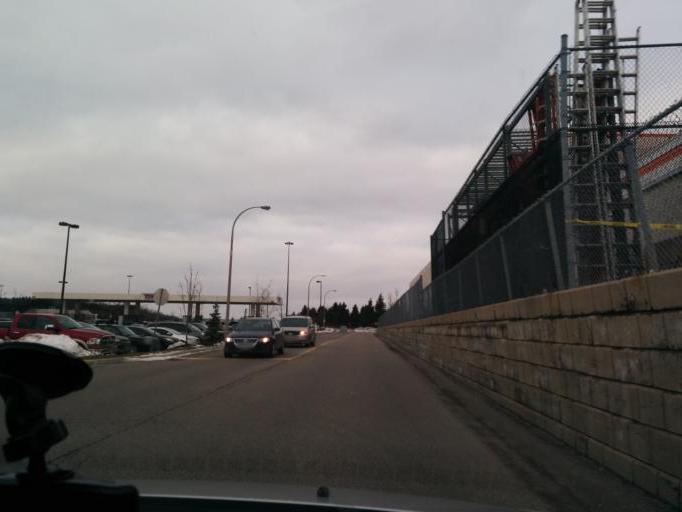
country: CA
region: Ontario
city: Ancaster
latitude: 43.2297
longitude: -79.9454
